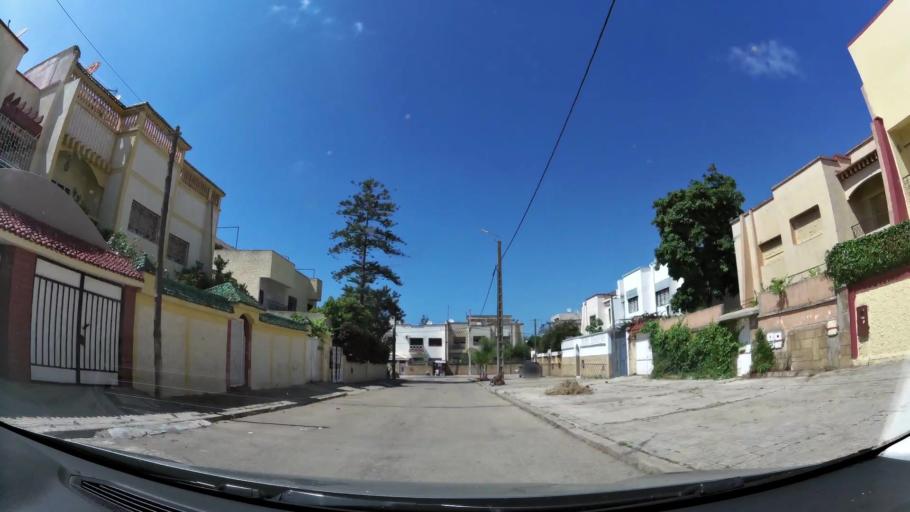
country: MA
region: Rabat-Sale-Zemmour-Zaer
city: Sale
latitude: 34.0416
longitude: -6.7863
